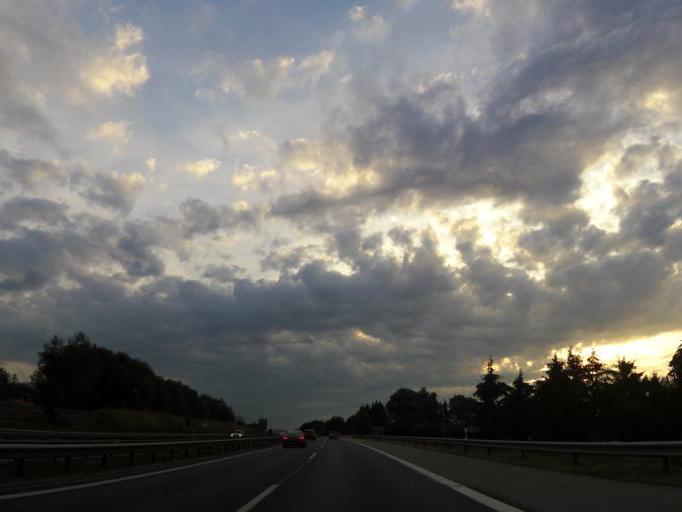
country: DE
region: Bavaria
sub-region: Upper Bavaria
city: Ubersee
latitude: 47.8389
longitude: 12.4828
